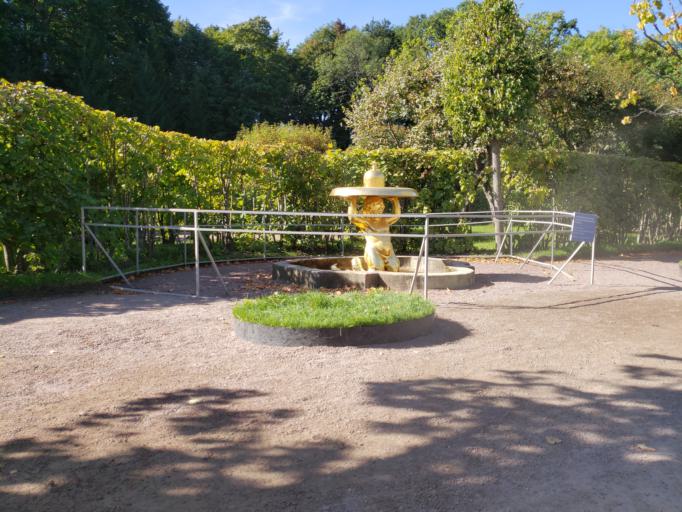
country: RU
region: St.-Petersburg
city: Peterhof
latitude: 59.8882
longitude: 29.8964
